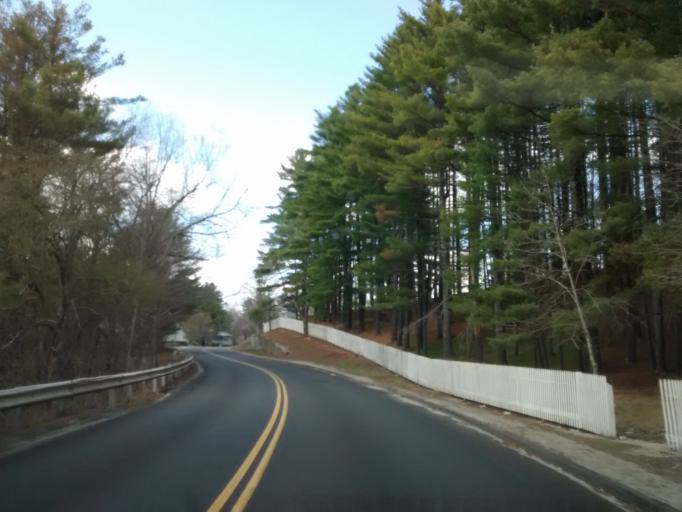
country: US
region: Massachusetts
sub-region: Worcester County
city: Upton
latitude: 42.1611
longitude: -71.6196
